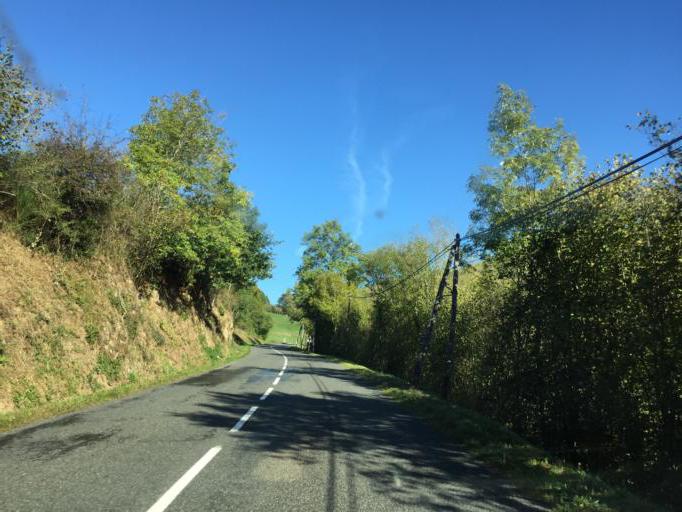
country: FR
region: Rhone-Alpes
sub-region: Departement du Rhone
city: Grandris
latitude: 46.0310
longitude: 4.5158
